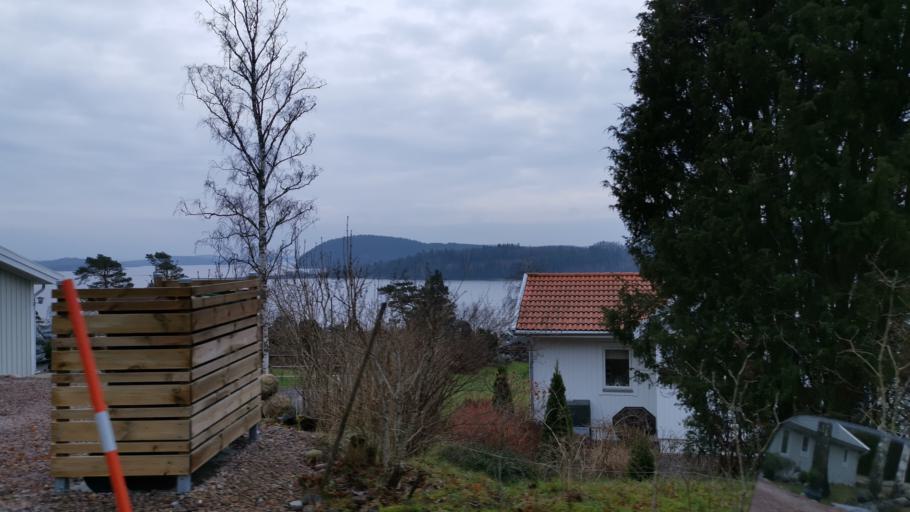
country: SE
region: Vaestra Goetaland
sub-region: Orust
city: Henan
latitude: 58.3394
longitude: 11.7207
